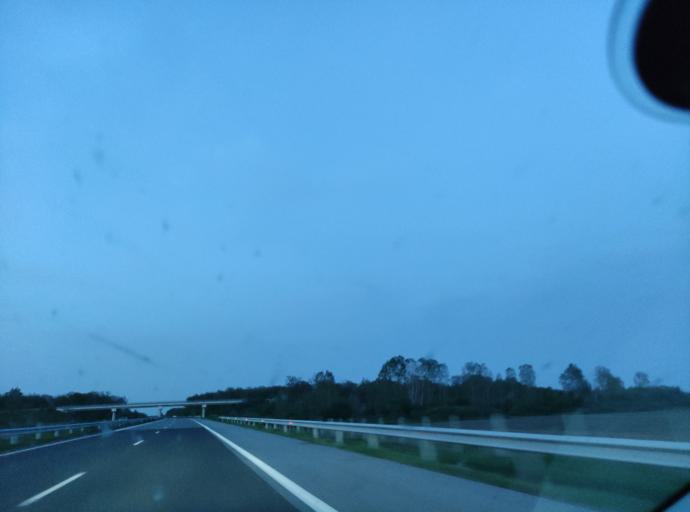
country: BG
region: Stara Zagora
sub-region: Obshtina Stara Zagora
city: Stara Zagora
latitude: 42.3514
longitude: 25.7357
